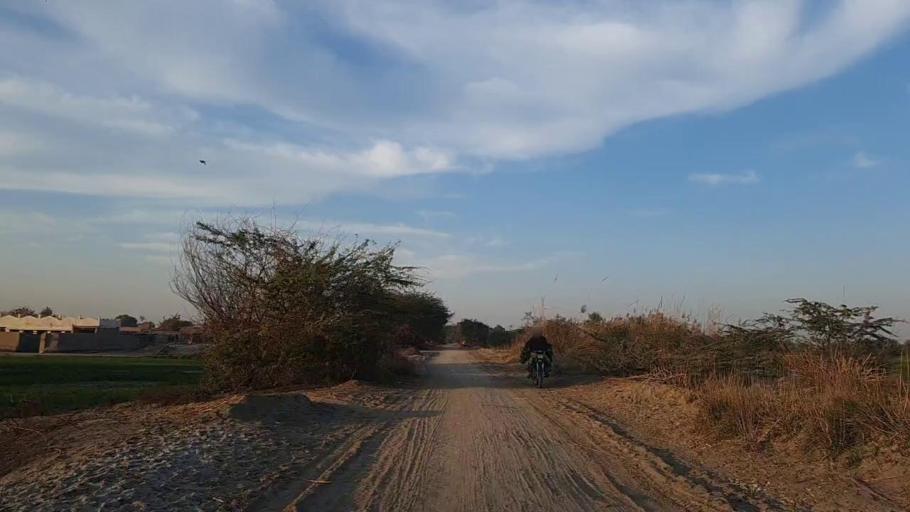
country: PK
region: Sindh
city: Bandhi
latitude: 26.6064
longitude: 68.3592
